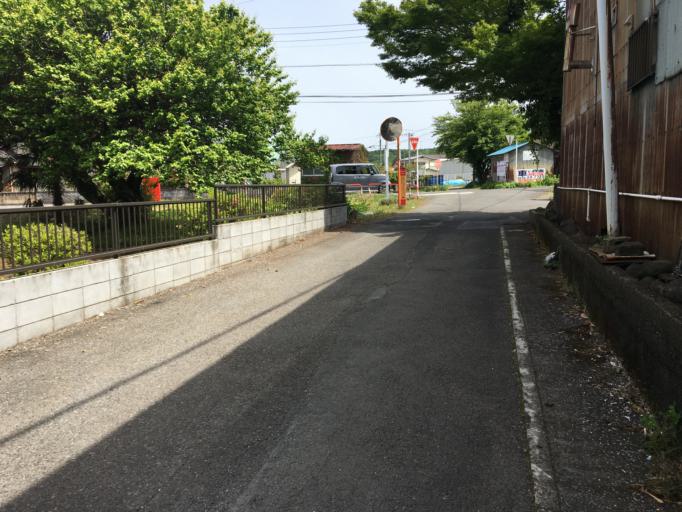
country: JP
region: Saitama
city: Hanno
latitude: 35.8891
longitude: 139.3203
